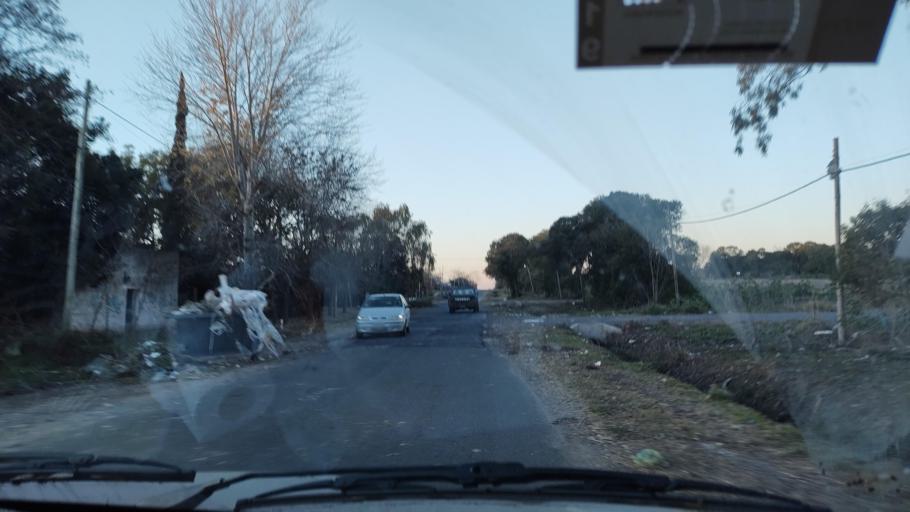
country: AR
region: Buenos Aires
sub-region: Partido de La Plata
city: La Plata
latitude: -34.9094
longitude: -58.0155
